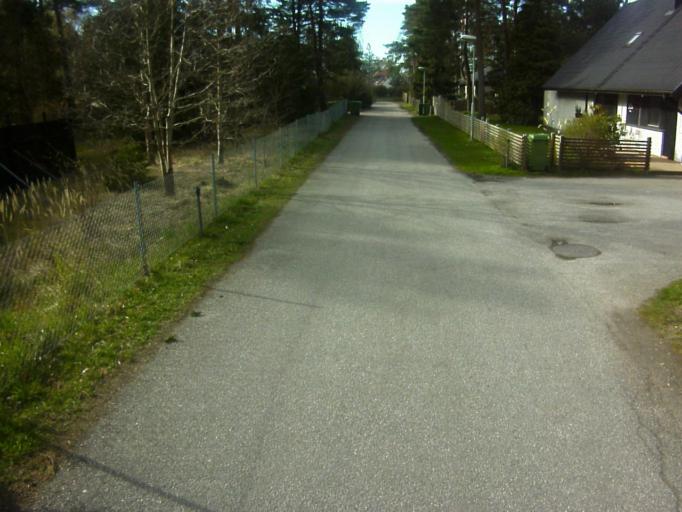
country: SE
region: Skane
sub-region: Kavlinge Kommun
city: Hofterup
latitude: 55.7985
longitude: 12.9802
